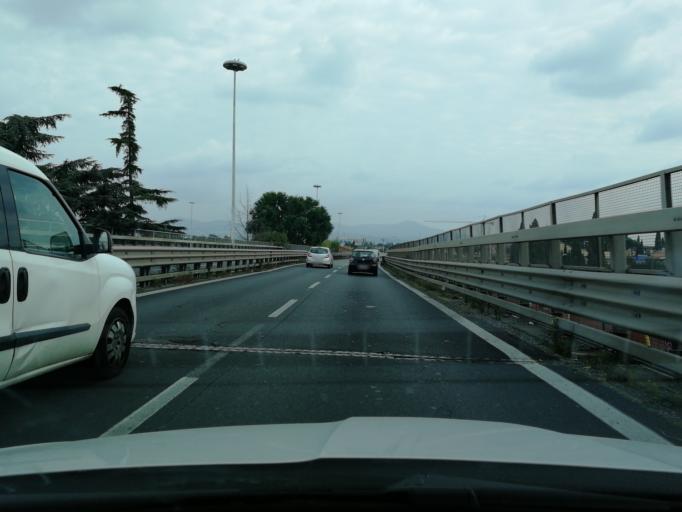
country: IT
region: Latium
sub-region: Citta metropolitana di Roma Capitale
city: Ciampino
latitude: 41.8431
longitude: 12.5836
